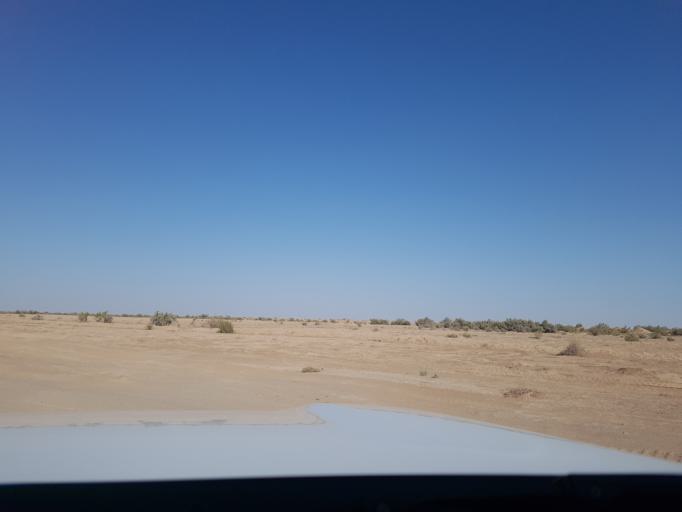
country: IR
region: Razavi Khorasan
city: Sarakhs
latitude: 36.8353
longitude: 61.3314
